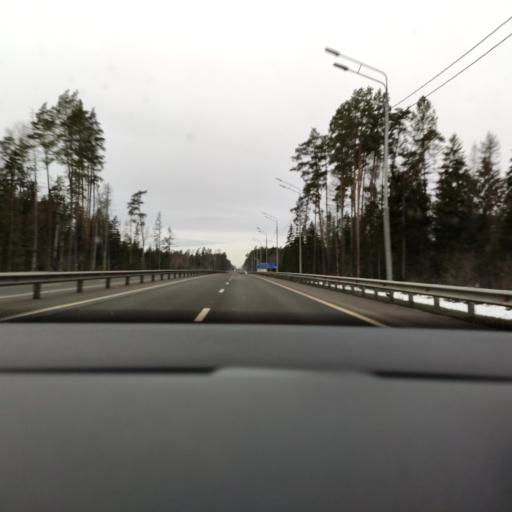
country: RU
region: Moskovskaya
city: Bol'shiye Vyazemy
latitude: 55.6648
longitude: 36.9411
